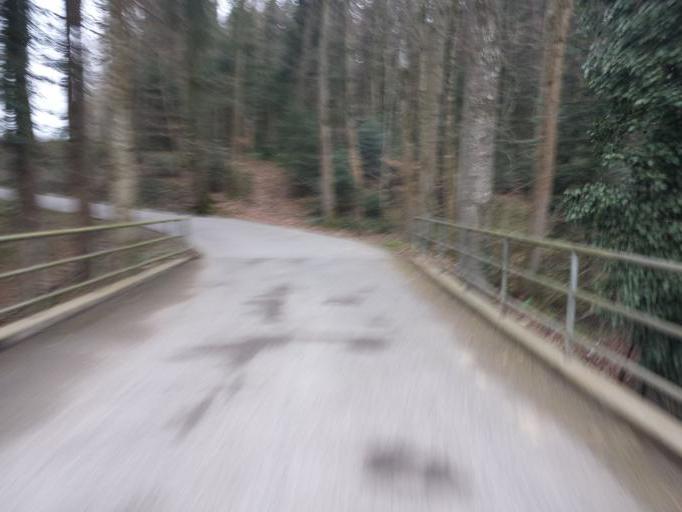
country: CH
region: Saint Gallen
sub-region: Wahlkreis St. Gallen
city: Muolen
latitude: 47.5512
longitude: 9.3366
